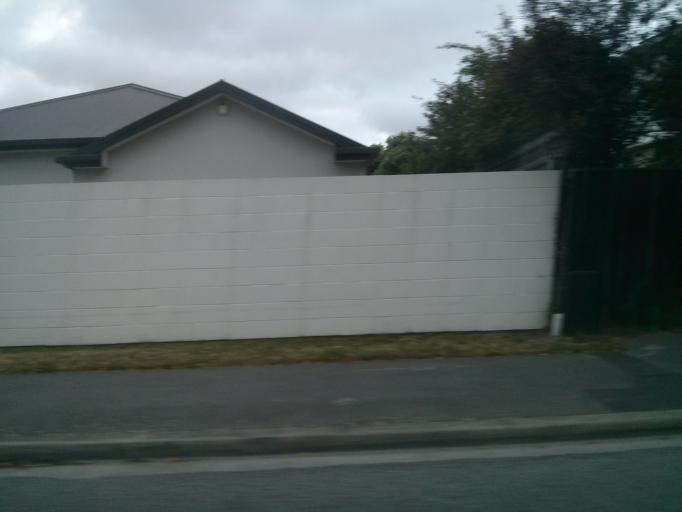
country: NZ
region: Canterbury
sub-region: Christchurch City
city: Christchurch
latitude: -43.5076
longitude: 172.6024
